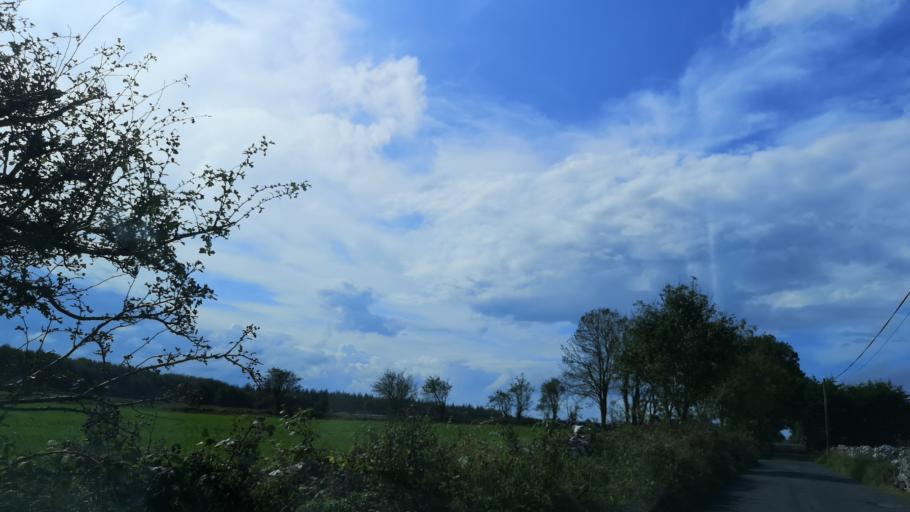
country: IE
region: Connaught
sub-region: County Galway
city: Athenry
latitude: 53.2958
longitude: -8.8329
